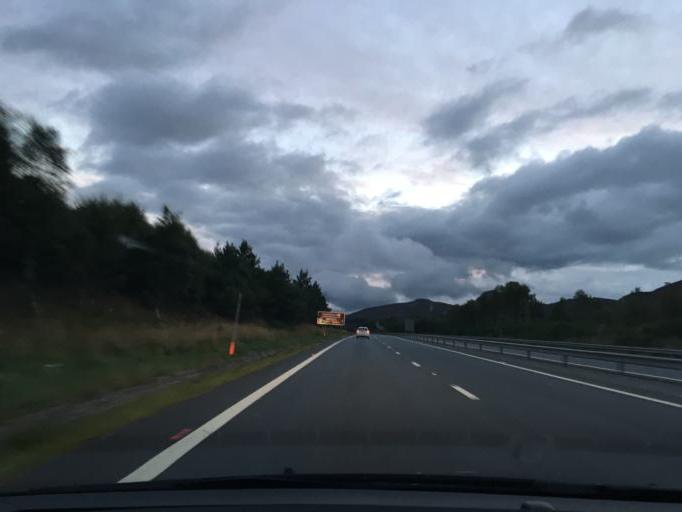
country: GB
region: Scotland
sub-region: Highland
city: Kingussie
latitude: 57.0134
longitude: -4.1633
